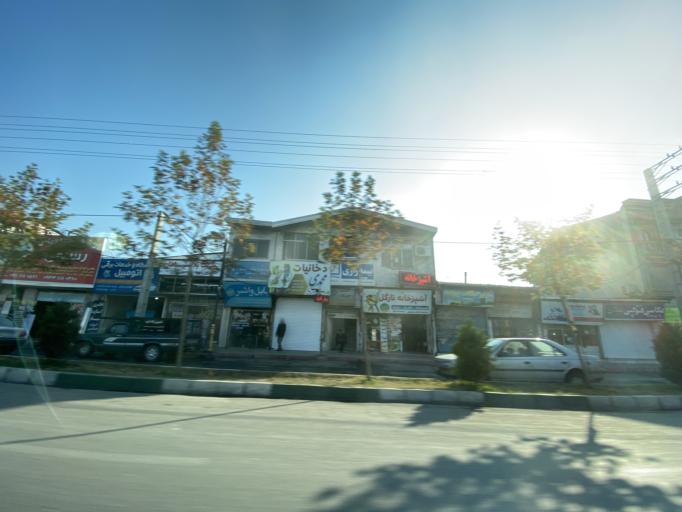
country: IR
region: Mazandaran
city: Babol
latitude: 36.5352
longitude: 52.6562
